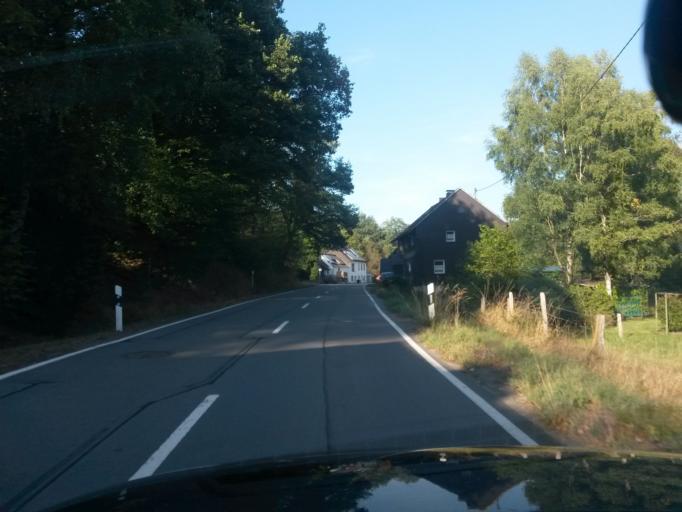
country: DE
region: North Rhine-Westphalia
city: Wiehl
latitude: 50.9627
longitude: 7.5707
